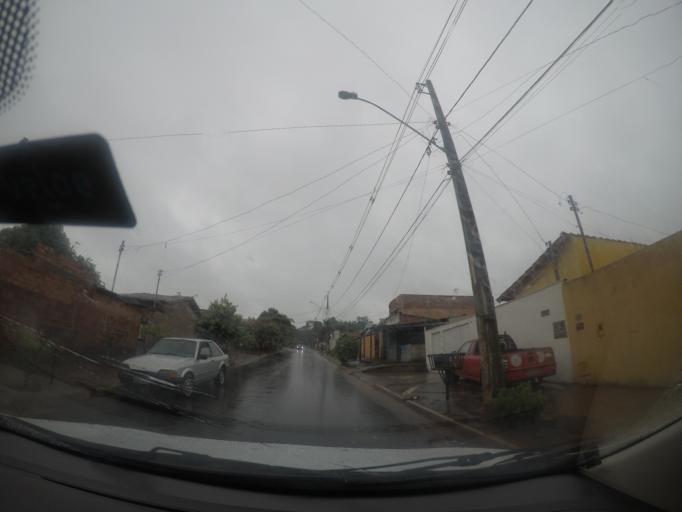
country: BR
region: Goias
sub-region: Goianira
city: Goianira
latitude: -16.5866
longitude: -49.3414
